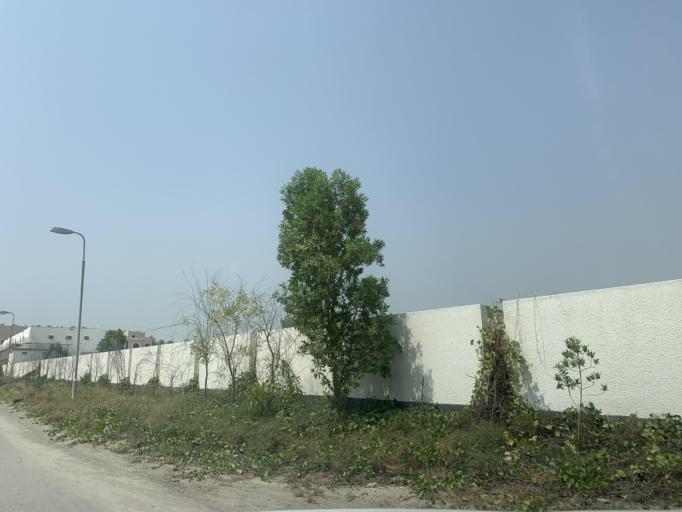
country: BH
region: Central Governorate
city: Madinat Hamad
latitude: 26.1613
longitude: 50.4545
